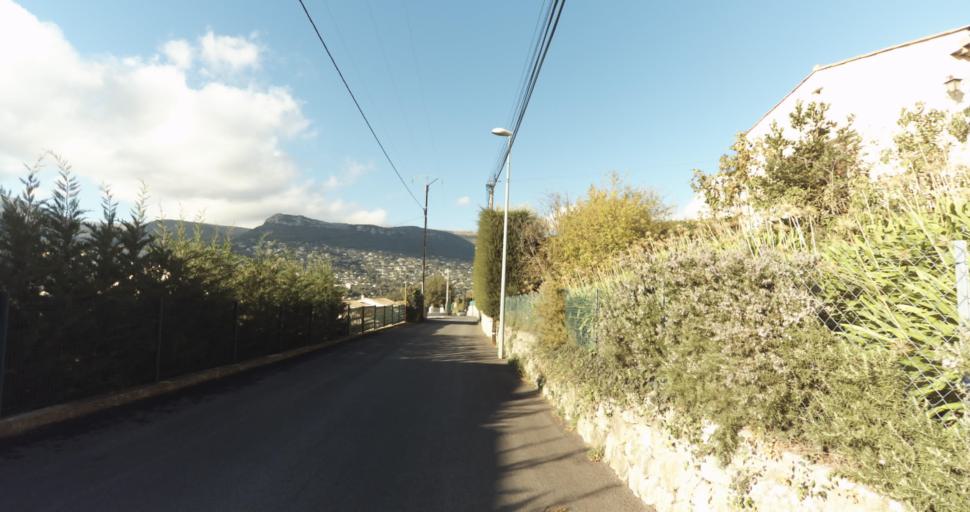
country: FR
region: Provence-Alpes-Cote d'Azur
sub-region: Departement des Alpes-Maritimes
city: La Gaude
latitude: 43.7143
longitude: 7.1337
